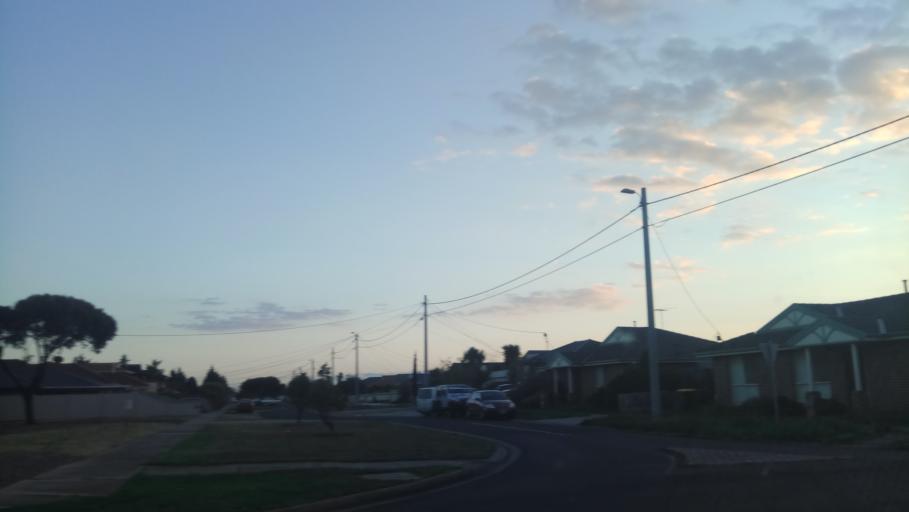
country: AU
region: Victoria
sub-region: Hobsons Bay
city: Altona Meadows
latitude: -37.8800
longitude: 144.7788
